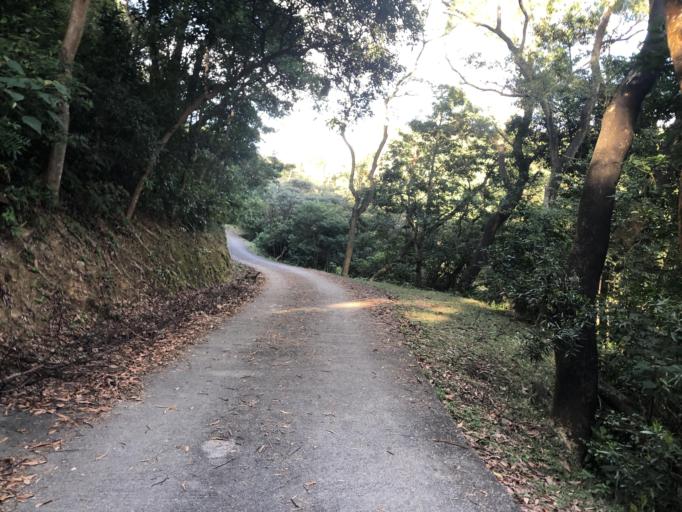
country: HK
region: Tsuen Wan
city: Tsuen Wan
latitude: 22.3912
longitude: 114.0855
